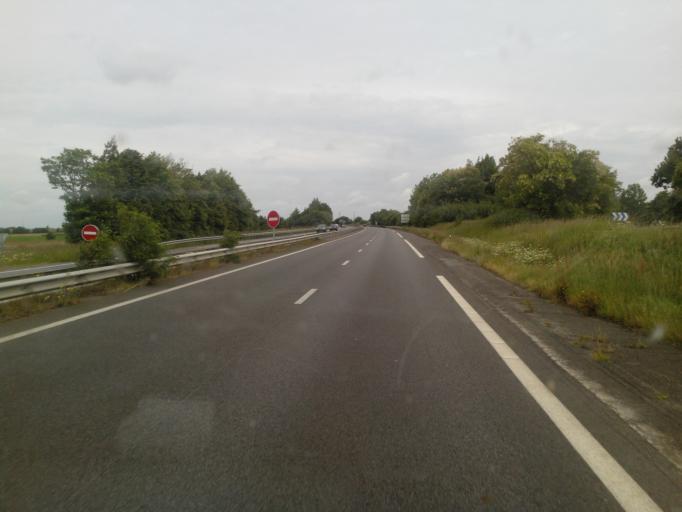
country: FR
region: Brittany
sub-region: Departement des Cotes-d'Armor
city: Broons
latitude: 48.3060
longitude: -2.2358
